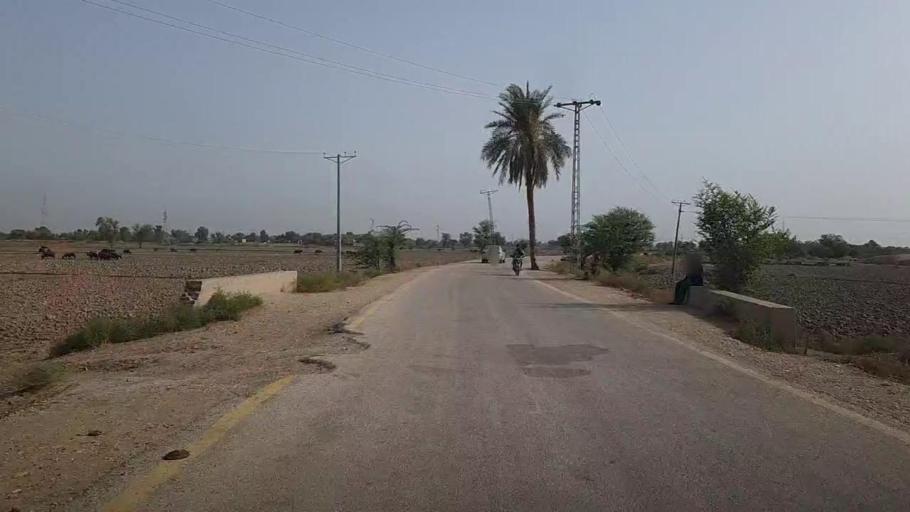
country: PK
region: Sindh
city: Khairpur Nathan Shah
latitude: 27.0994
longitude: 67.7554
